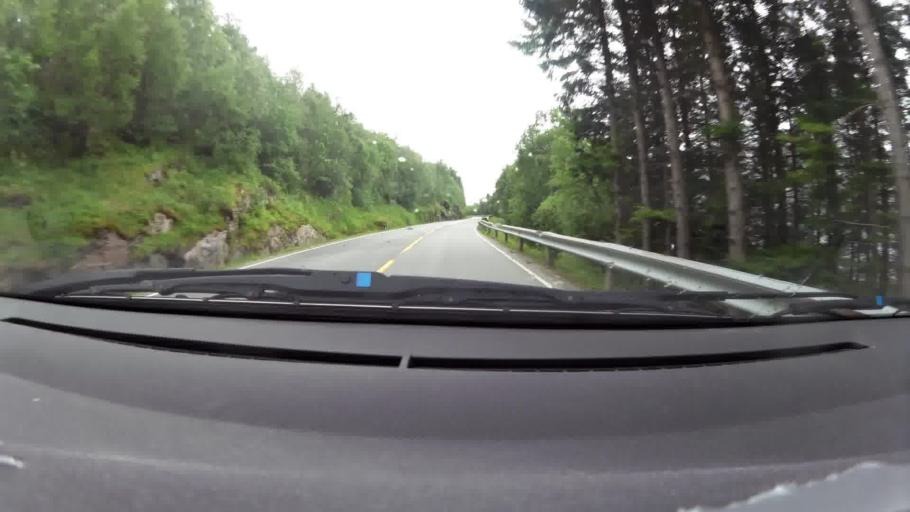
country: NO
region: More og Romsdal
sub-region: Gjemnes
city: Batnfjordsora
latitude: 62.9176
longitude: 7.7443
